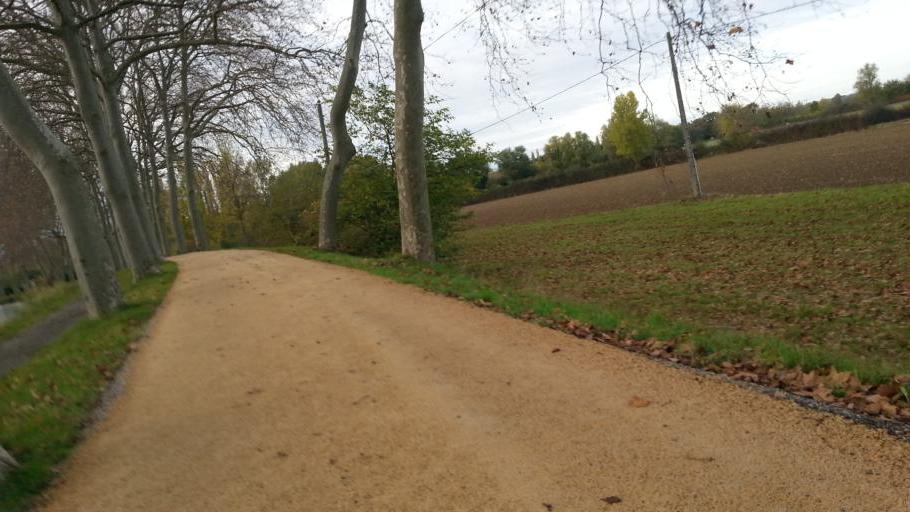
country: FR
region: Midi-Pyrenees
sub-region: Departement de la Haute-Garonne
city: Auzeville-Tolosane
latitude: 43.5385
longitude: 1.4998
